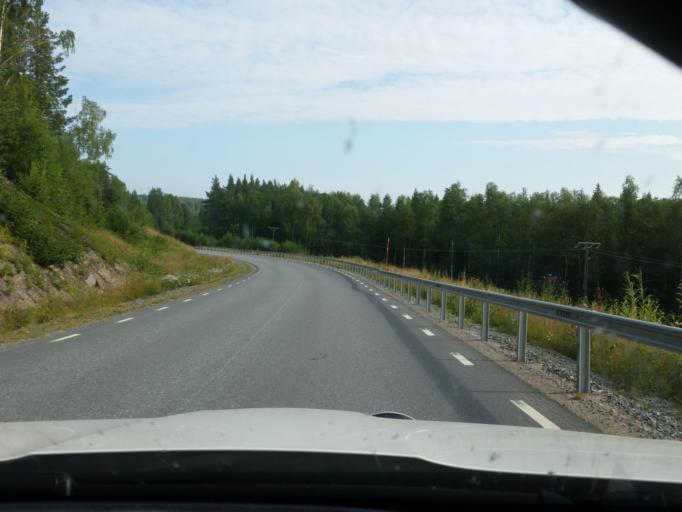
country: SE
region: Norrbotten
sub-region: Alvsbyns Kommun
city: AElvsbyn
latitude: 65.6601
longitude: 20.8773
